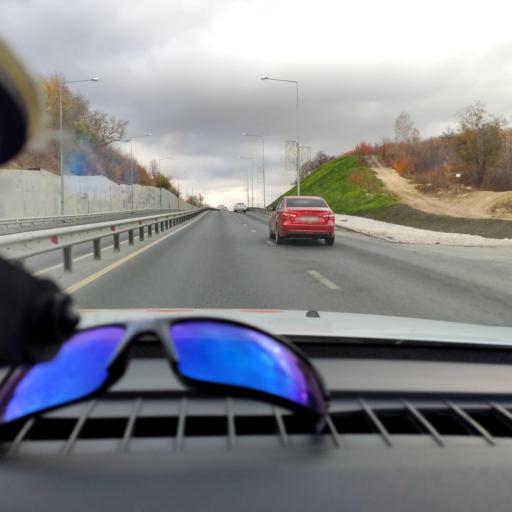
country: RU
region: Samara
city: Volzhskiy
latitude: 53.3712
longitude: 50.1838
